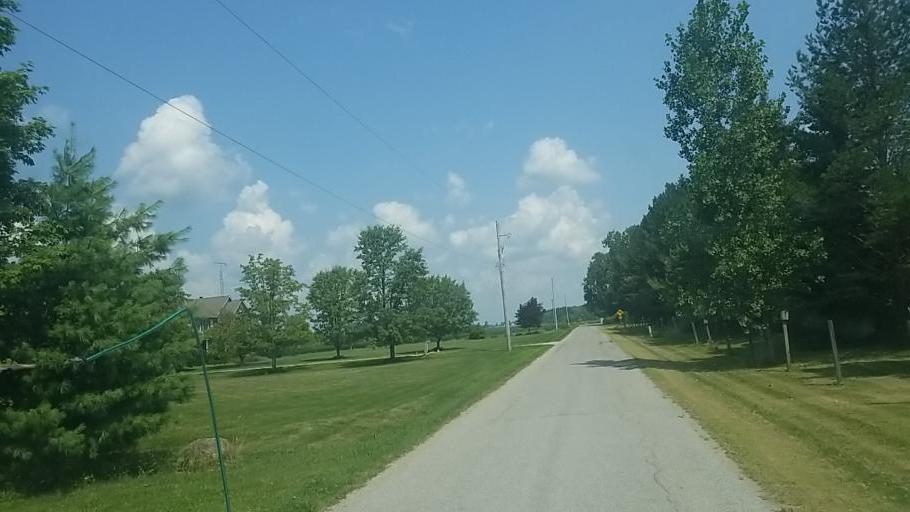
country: US
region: Ohio
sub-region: Crawford County
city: Crestline
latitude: 40.8060
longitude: -82.7260
